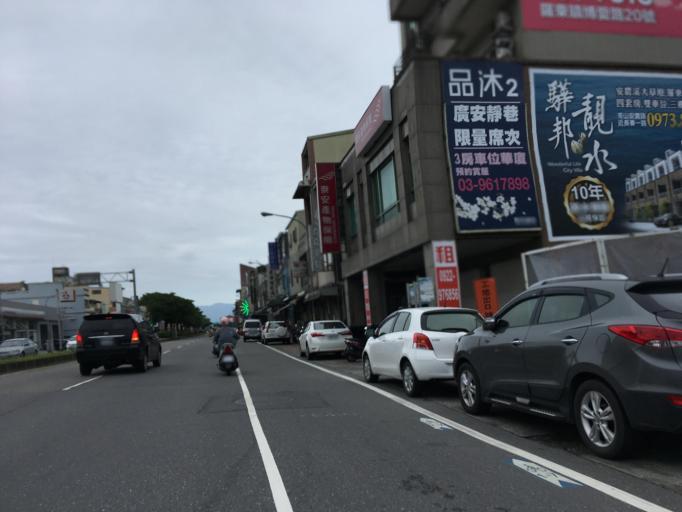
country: TW
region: Taiwan
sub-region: Yilan
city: Yilan
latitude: 24.6949
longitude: 121.7696
